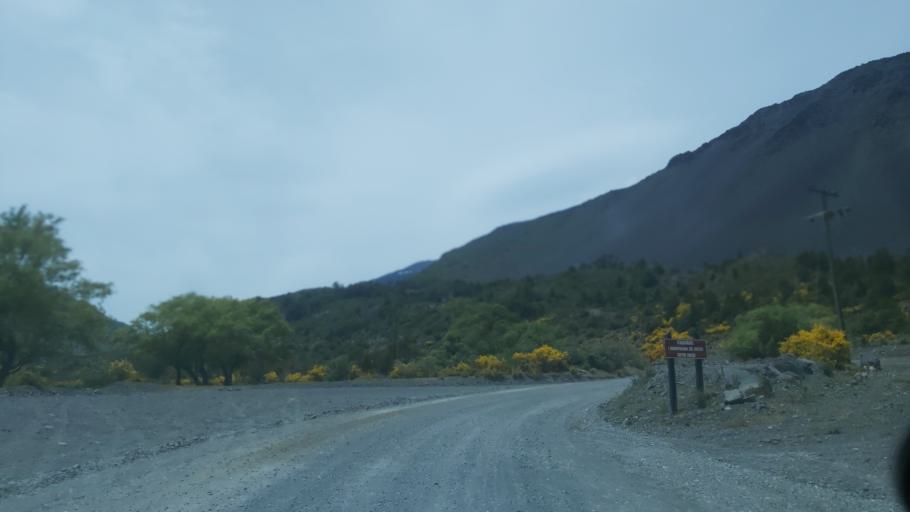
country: AR
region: Neuquen
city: Andacollo
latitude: -37.3922
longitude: -71.4085
